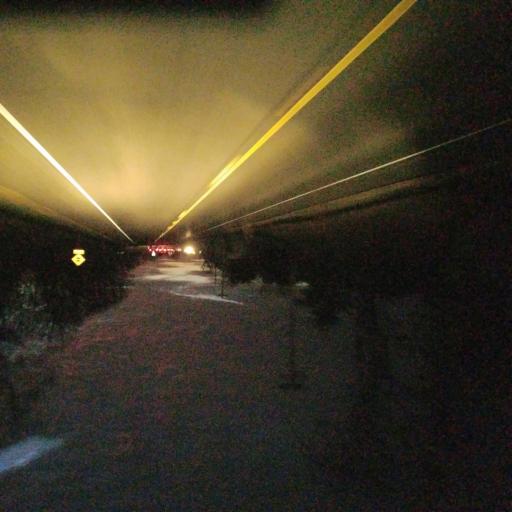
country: US
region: Illinois
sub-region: Peoria County
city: Elmwood
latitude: 40.6980
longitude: -89.9032
